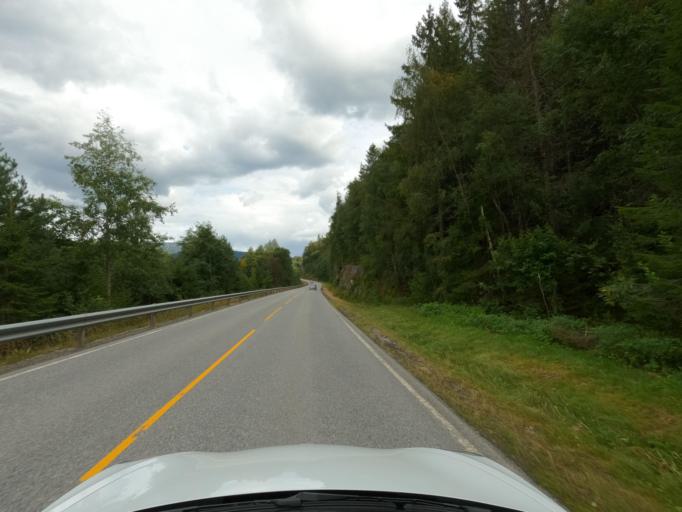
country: NO
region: Telemark
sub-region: Hjartdal
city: Sauland
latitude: 59.8352
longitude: 8.9627
